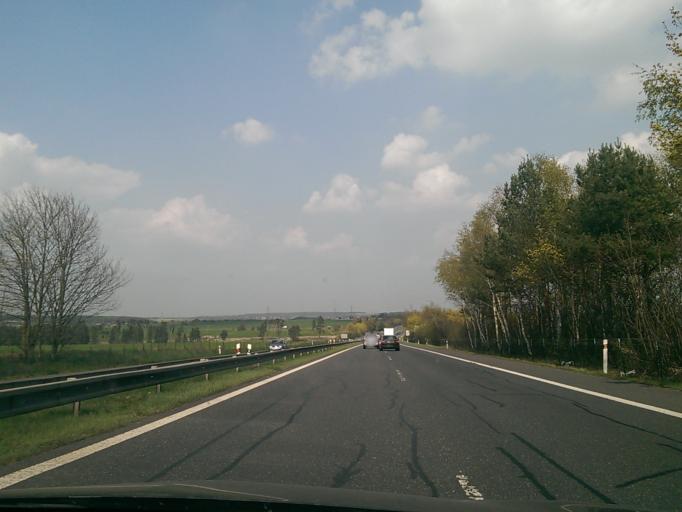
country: CZ
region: Central Bohemia
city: Celakovice
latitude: 50.2442
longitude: 14.7466
